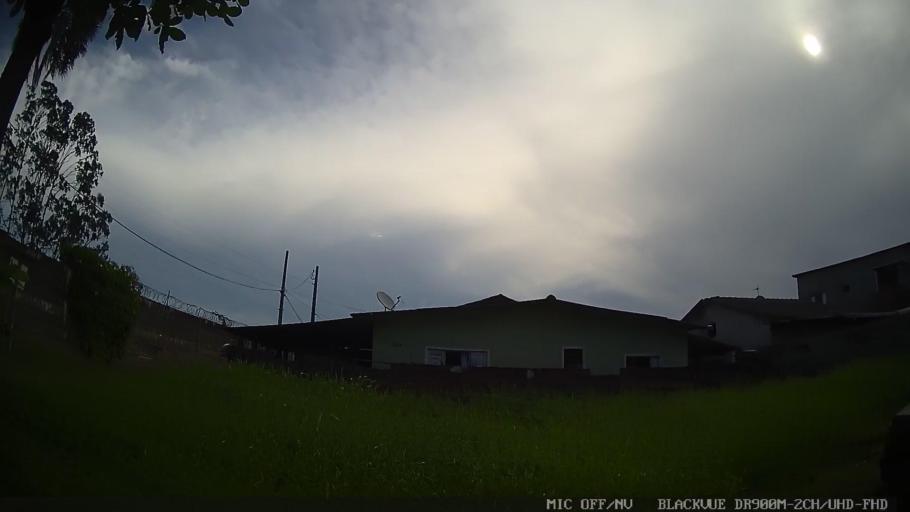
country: BR
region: Sao Paulo
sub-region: Iguape
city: Iguape
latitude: -24.7014
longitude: -47.5549
